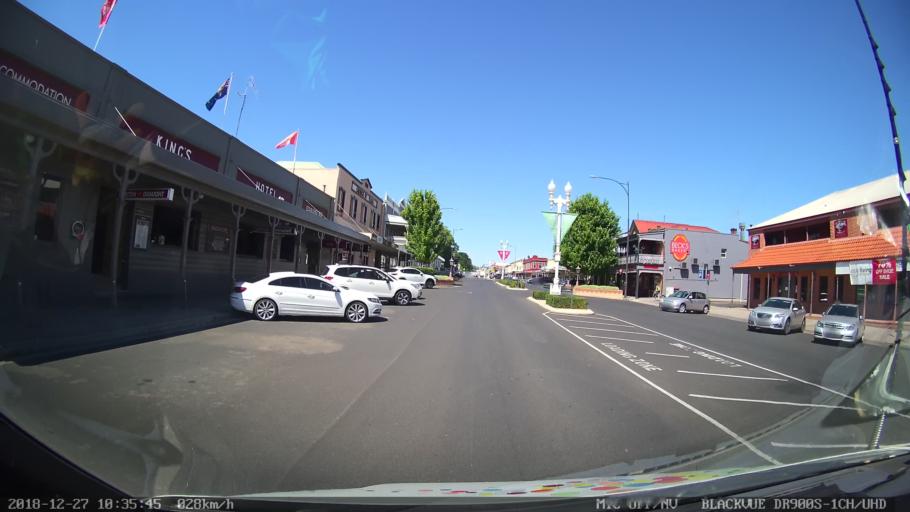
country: AU
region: New South Wales
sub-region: Bathurst Regional
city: Bathurst
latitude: -33.4150
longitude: 149.5812
